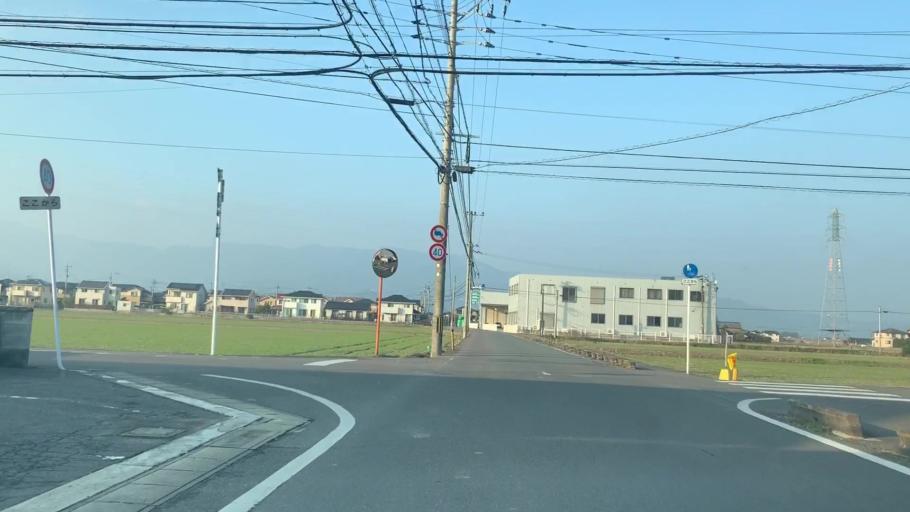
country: JP
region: Saga Prefecture
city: Saga-shi
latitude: 33.2666
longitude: 130.2305
